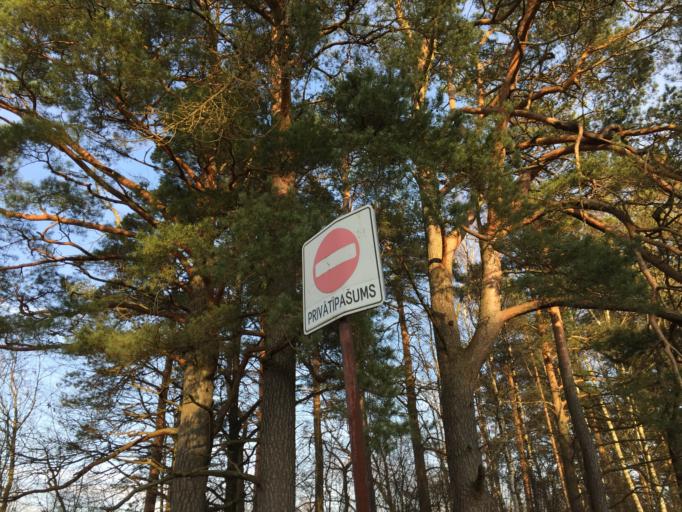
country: LV
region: Stopini
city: Ulbroka
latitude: 56.9635
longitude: 24.2857
